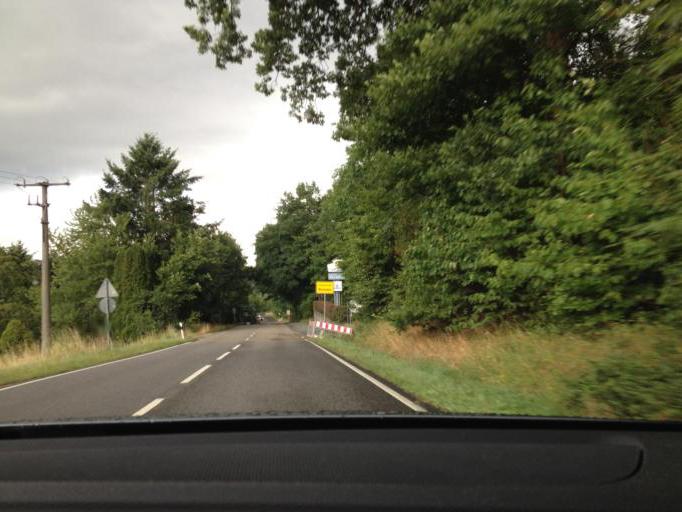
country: DE
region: Hesse
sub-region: Regierungsbezirk Darmstadt
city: Wiesbaden
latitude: 50.0944
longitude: 8.1947
